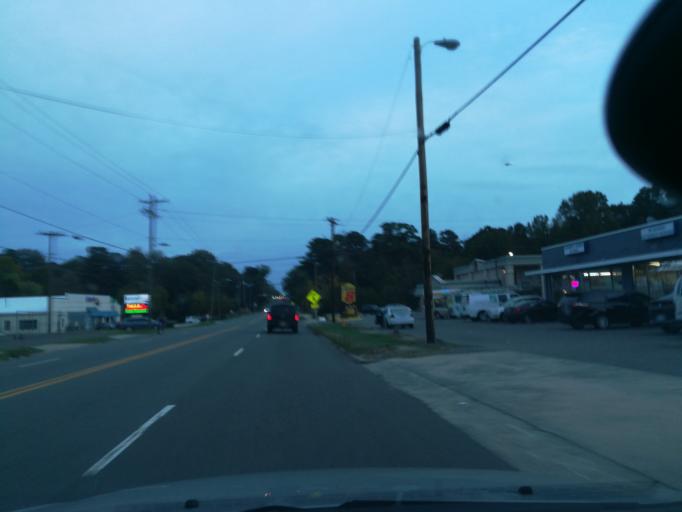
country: US
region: North Carolina
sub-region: Durham County
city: Durham
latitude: 36.0267
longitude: -78.9230
